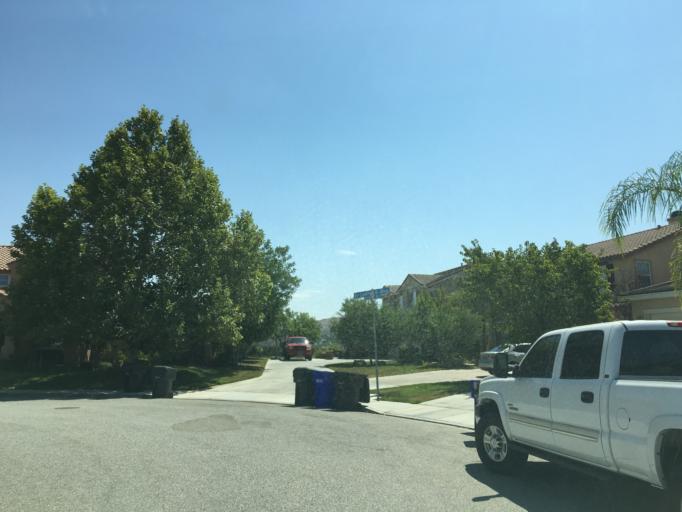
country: US
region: California
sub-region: Los Angeles County
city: Valencia
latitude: 34.4703
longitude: -118.5581
